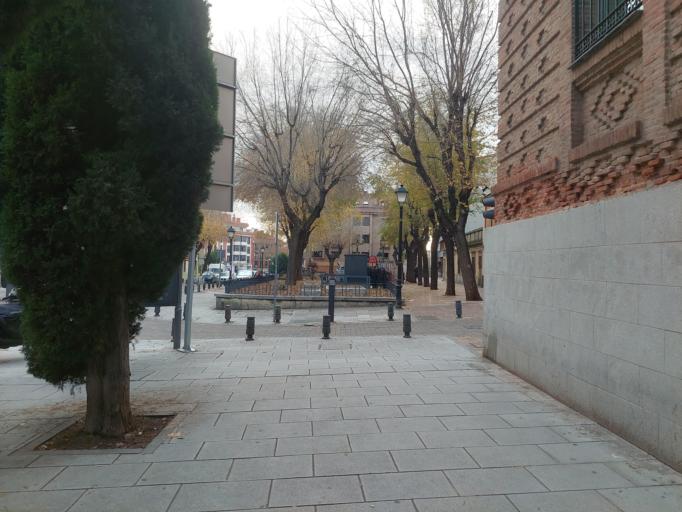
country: ES
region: Madrid
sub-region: Provincia de Madrid
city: Leganes
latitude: 40.3273
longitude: -3.7663
